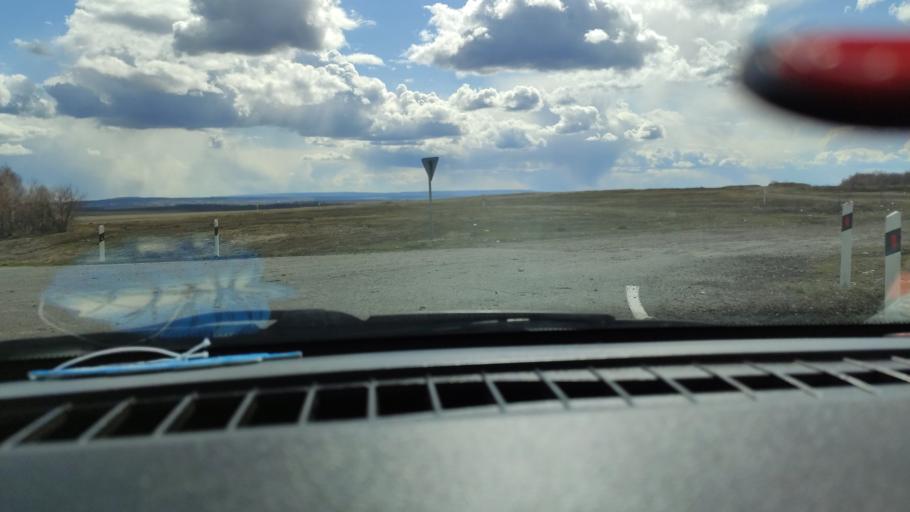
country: RU
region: Saratov
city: Dukhovnitskoye
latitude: 52.7858
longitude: 48.2332
